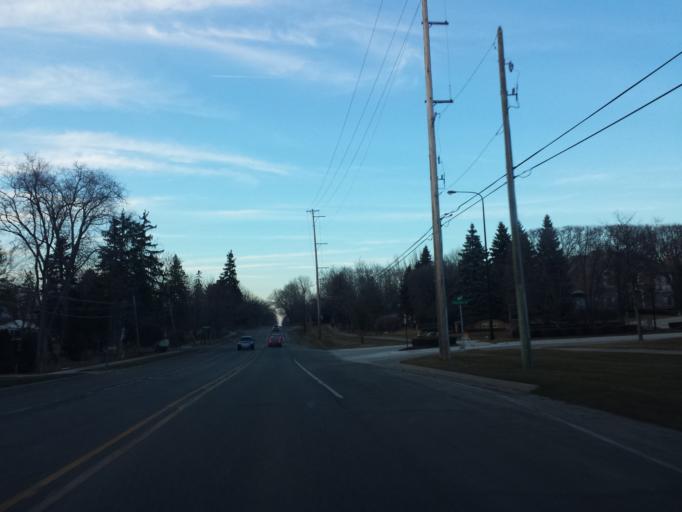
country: US
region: Michigan
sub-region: Oakland County
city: Bloomfield Hills
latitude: 42.5937
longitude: -83.2080
